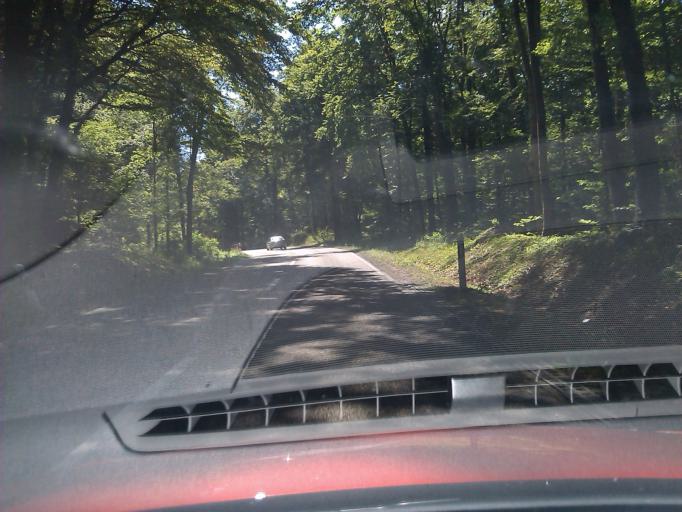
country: DE
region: Baden-Wuerttemberg
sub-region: Regierungsbezirk Stuttgart
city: Schwaigern
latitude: 49.1222
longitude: 9.0684
